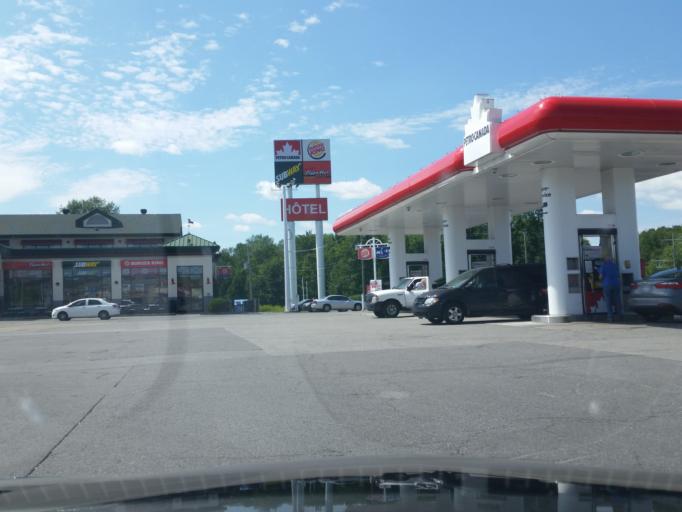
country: CA
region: Quebec
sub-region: Monteregie
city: Rigaud
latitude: 45.4614
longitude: -74.2272
